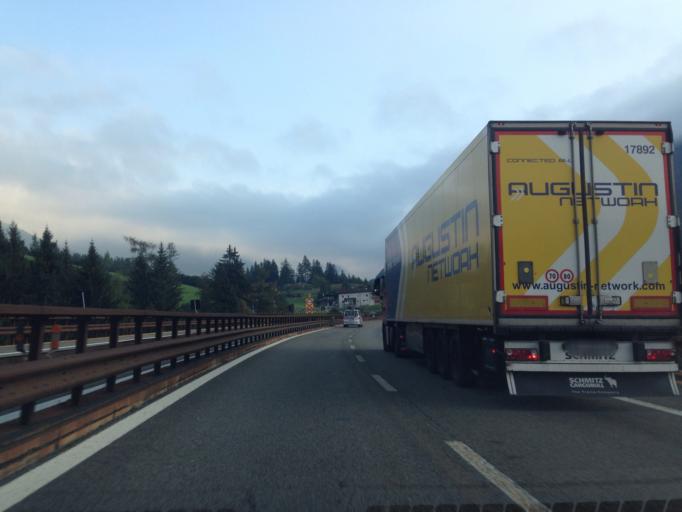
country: IT
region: Trentino-Alto Adige
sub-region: Bolzano
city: Brennero - Brenner
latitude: 46.9242
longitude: 11.4434
